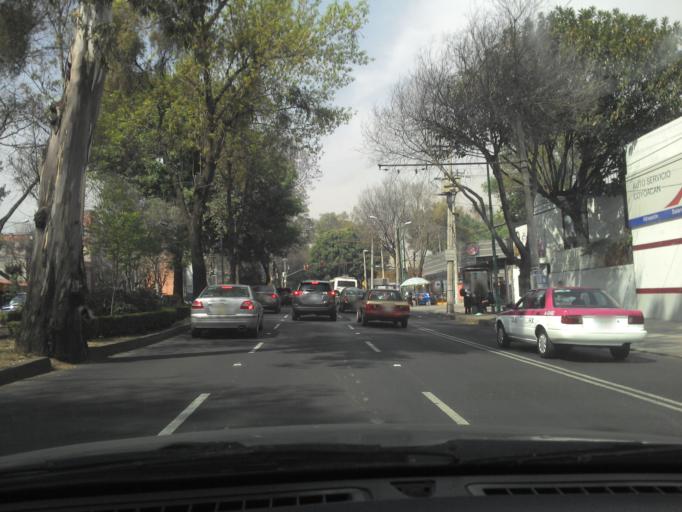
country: MX
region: Mexico City
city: Coyoacan
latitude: 19.3441
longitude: -99.1583
